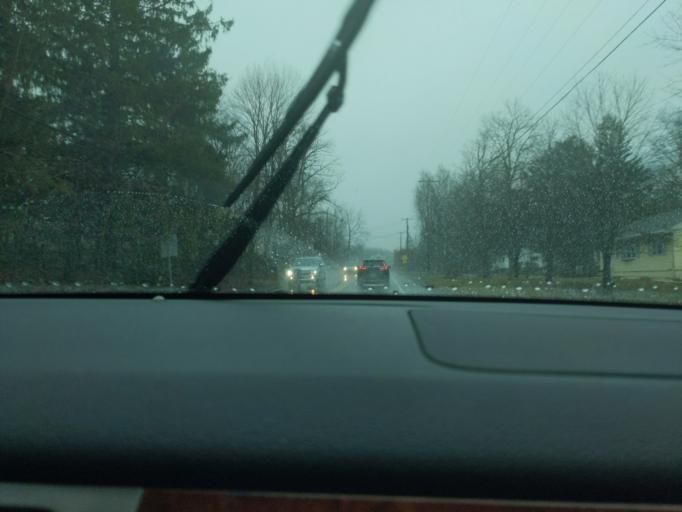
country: US
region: Pennsylvania
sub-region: Bucks County
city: Quakertown
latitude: 40.4326
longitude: -75.3002
